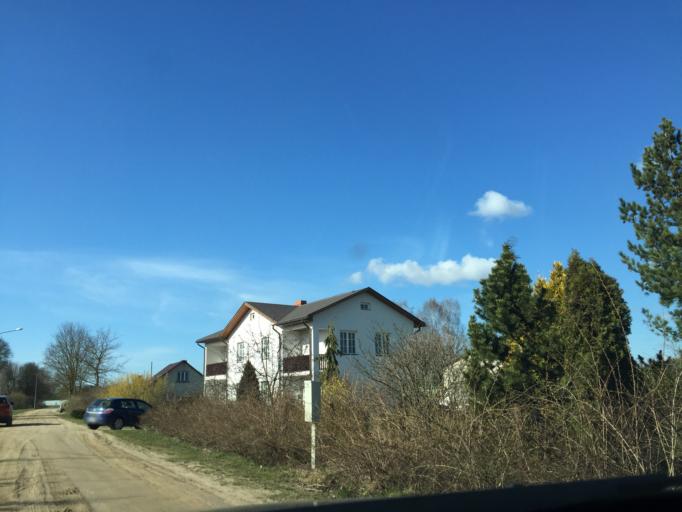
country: LV
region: Kekava
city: Kekava
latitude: 56.8467
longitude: 24.2048
